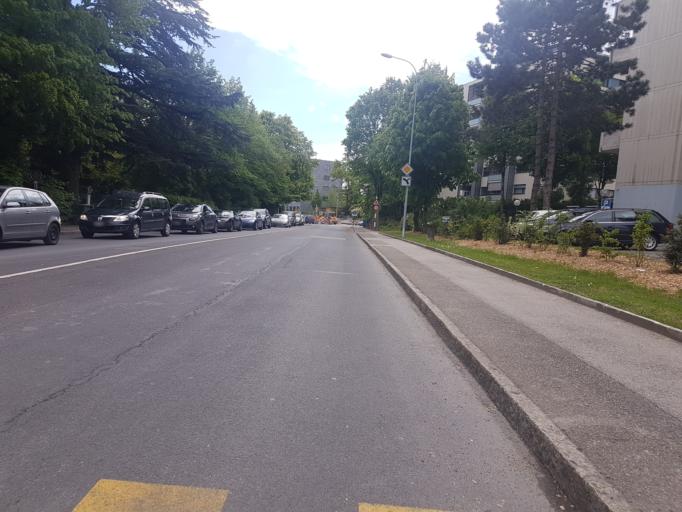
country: CH
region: Geneva
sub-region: Geneva
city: Versoix
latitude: 46.2833
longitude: 6.1658
